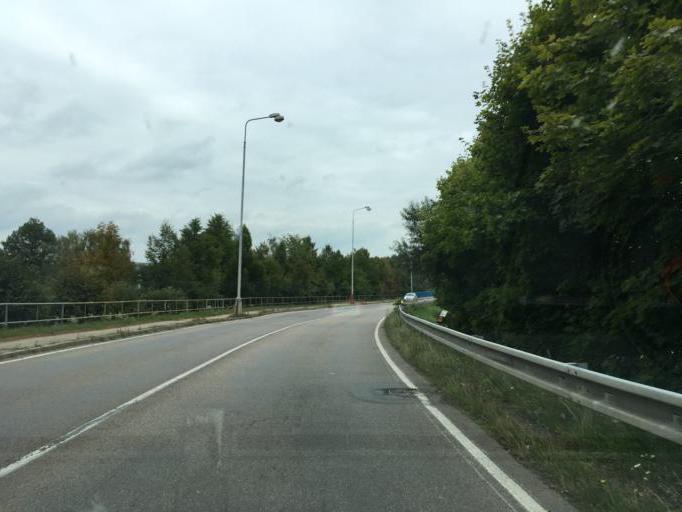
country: CZ
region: Central Bohemia
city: Vlasim
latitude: 49.7101
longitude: 14.8962
